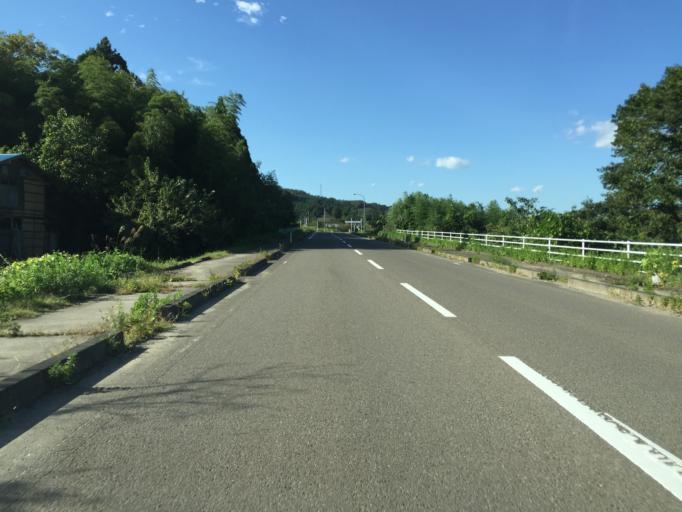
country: JP
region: Miyagi
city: Marumori
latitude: 37.8883
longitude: 140.7731
